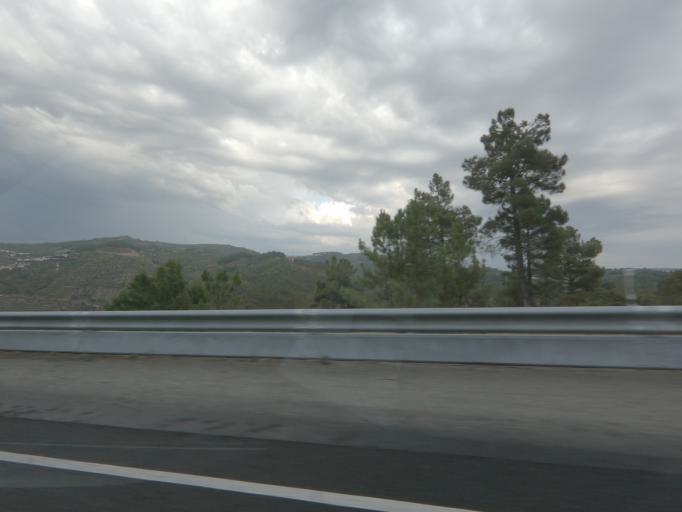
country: PT
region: Viseu
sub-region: Lamego
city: Lamego
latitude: 41.0974
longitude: -7.7813
